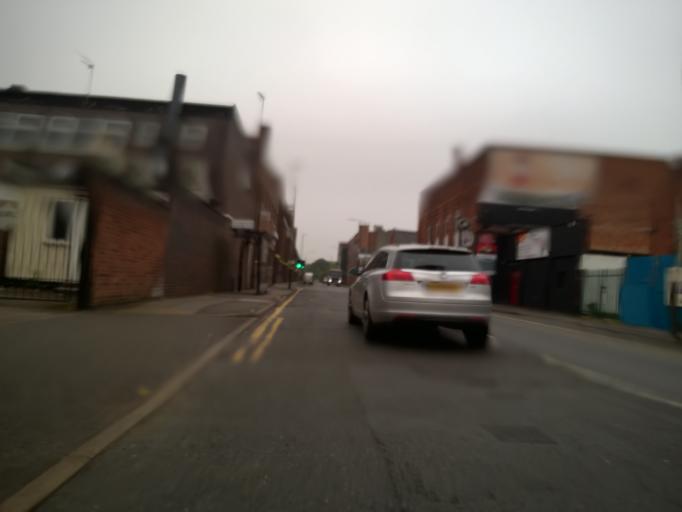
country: GB
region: England
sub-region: City of Leicester
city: Leicester
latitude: 52.6374
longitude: -1.1009
